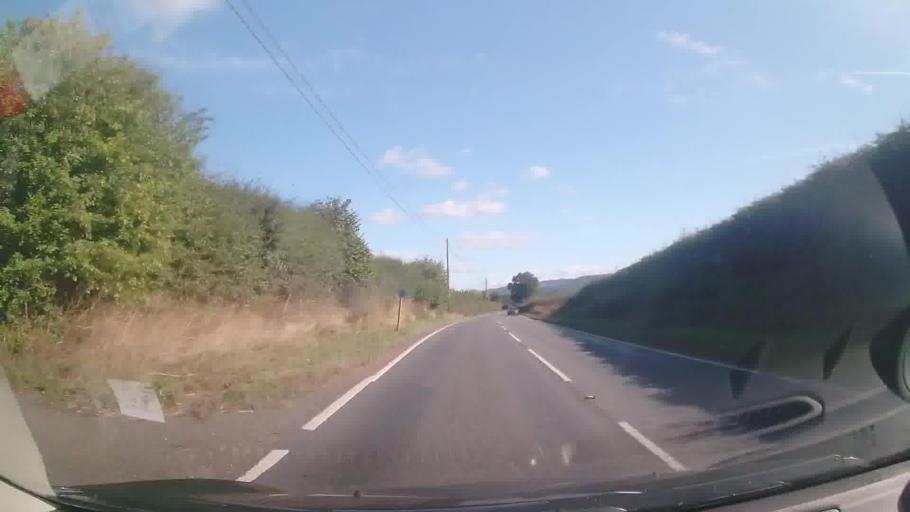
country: GB
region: Wales
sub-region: Sir Powys
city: Hay
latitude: 52.0159
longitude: -3.2323
